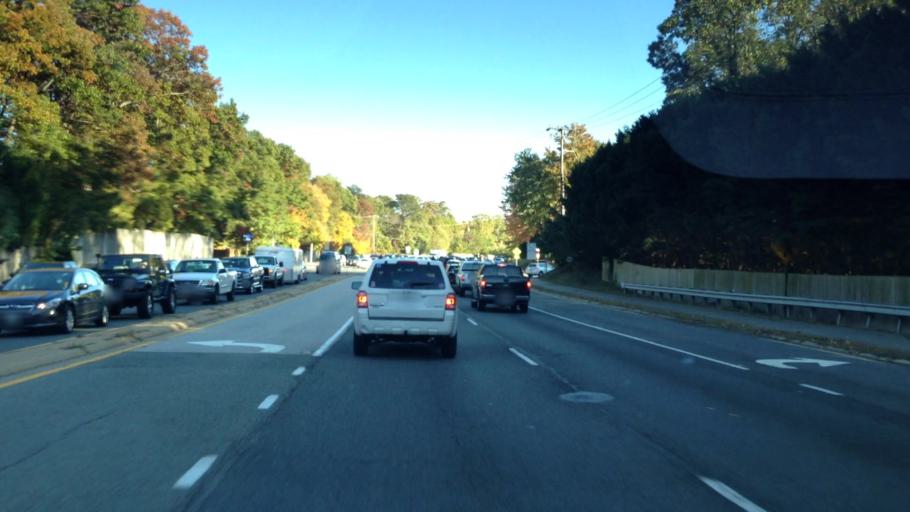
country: US
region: Virginia
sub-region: Fairfax County
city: Burke
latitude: 38.7495
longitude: -77.2620
